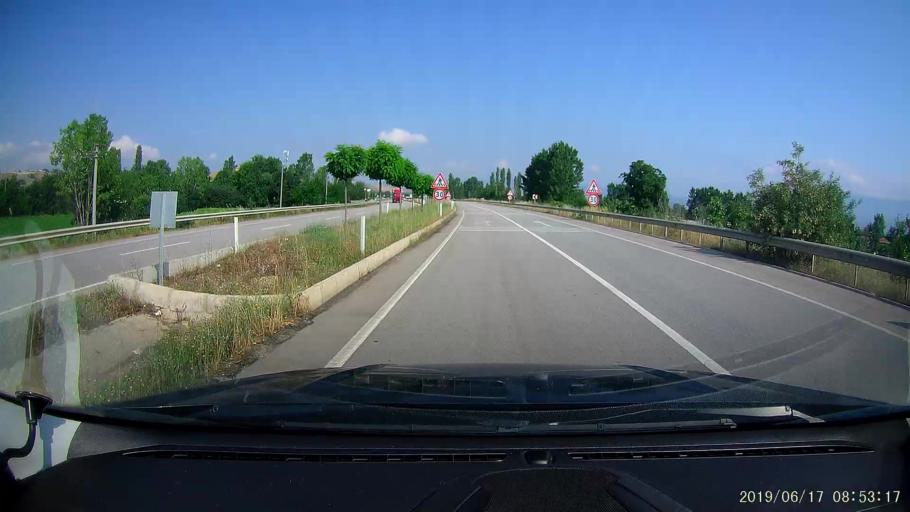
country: TR
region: Tokat
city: Erbaa
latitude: 40.7084
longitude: 36.4838
